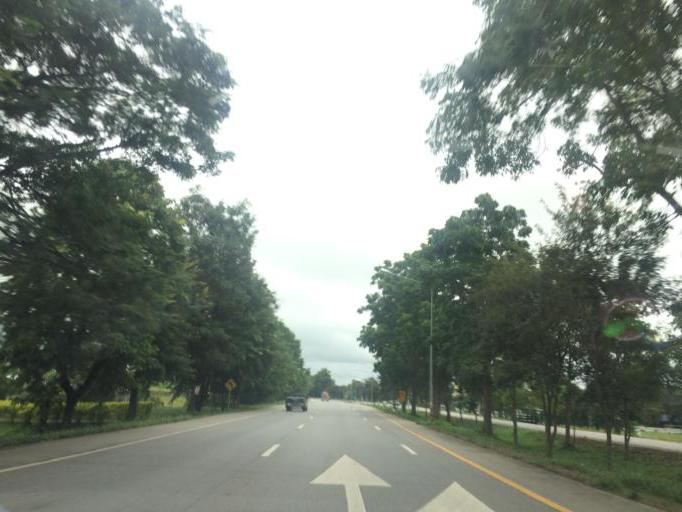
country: TH
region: Chiang Rai
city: Mae Lao
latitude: 19.7975
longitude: 99.7517
